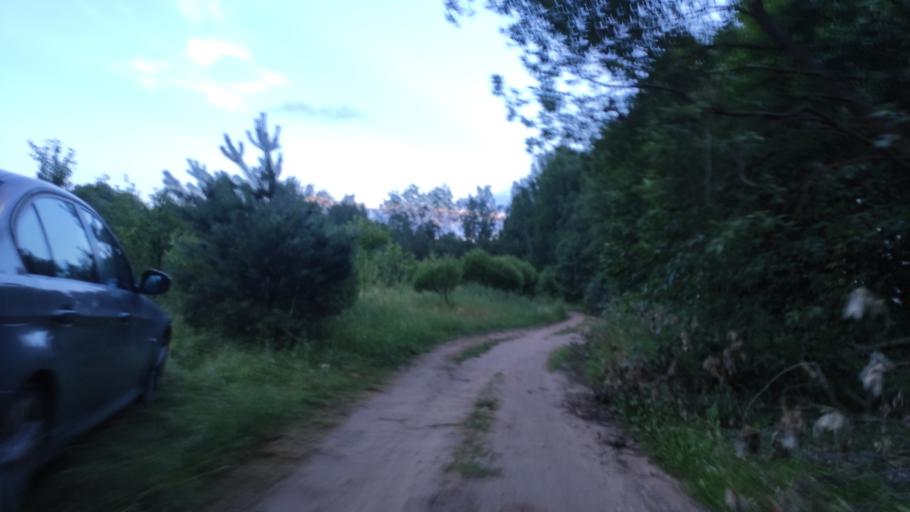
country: BY
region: Minsk
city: Zhdanovichy
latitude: 53.9502
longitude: 27.4727
